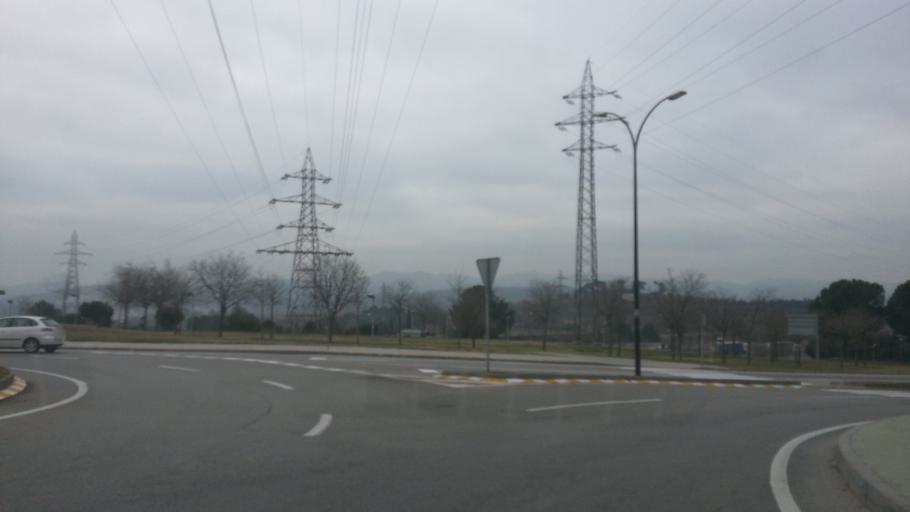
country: ES
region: Catalonia
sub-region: Provincia de Barcelona
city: Barbera del Valles
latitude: 41.4996
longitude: 2.1145
